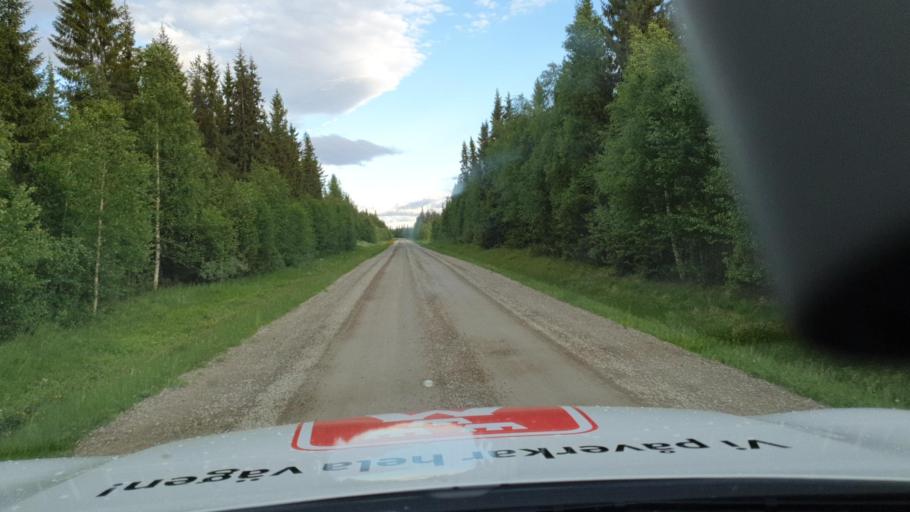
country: SE
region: Vaesterbotten
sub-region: Storumans Kommun
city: Storuman
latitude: 64.7244
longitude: 17.0750
